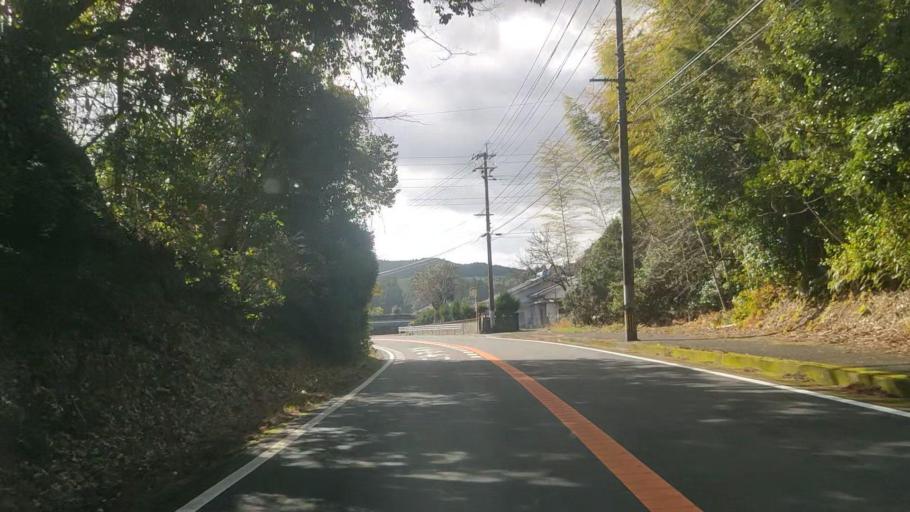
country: JP
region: Kagoshima
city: Okuchi-shinohara
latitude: 31.9347
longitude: 130.7035
